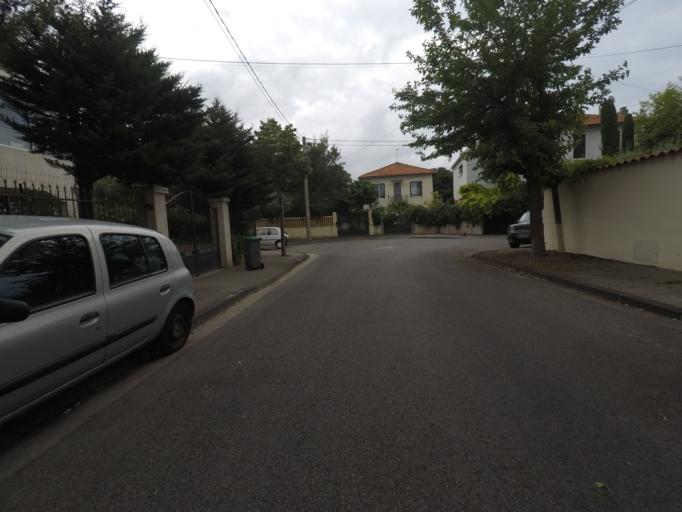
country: FR
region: Provence-Alpes-Cote d'Azur
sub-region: Departement des Bouches-du-Rhone
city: Marseille 08
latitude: 43.2605
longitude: 5.3899
